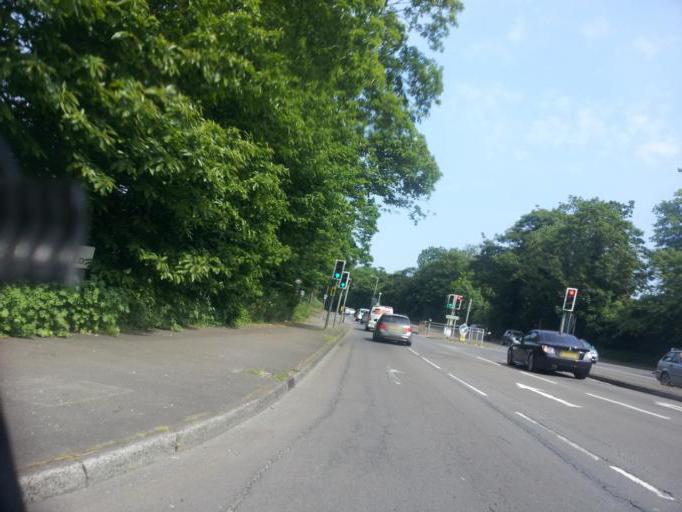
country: GB
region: England
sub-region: Kent
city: Larkfield
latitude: 51.2981
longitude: 0.4312
